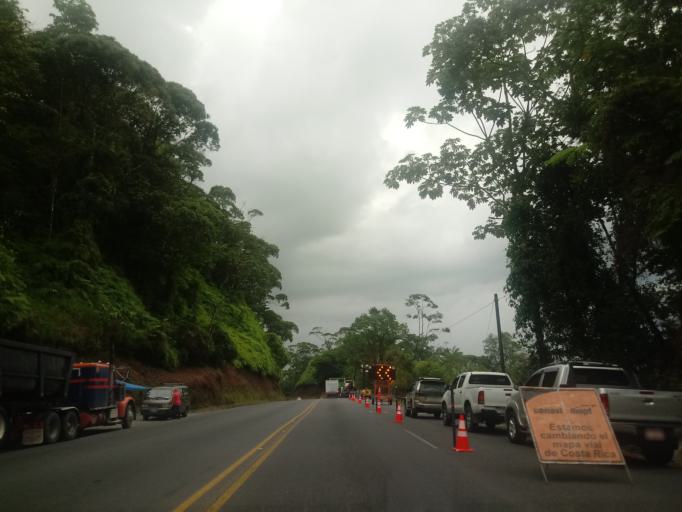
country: CR
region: San Jose
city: Dulce Nombre de Jesus
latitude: 10.1788
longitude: -83.9239
